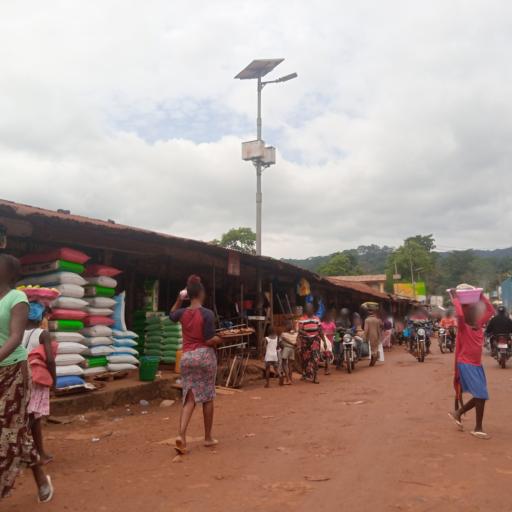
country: SL
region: Eastern Province
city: Kenema
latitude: 7.8762
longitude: -11.1935
